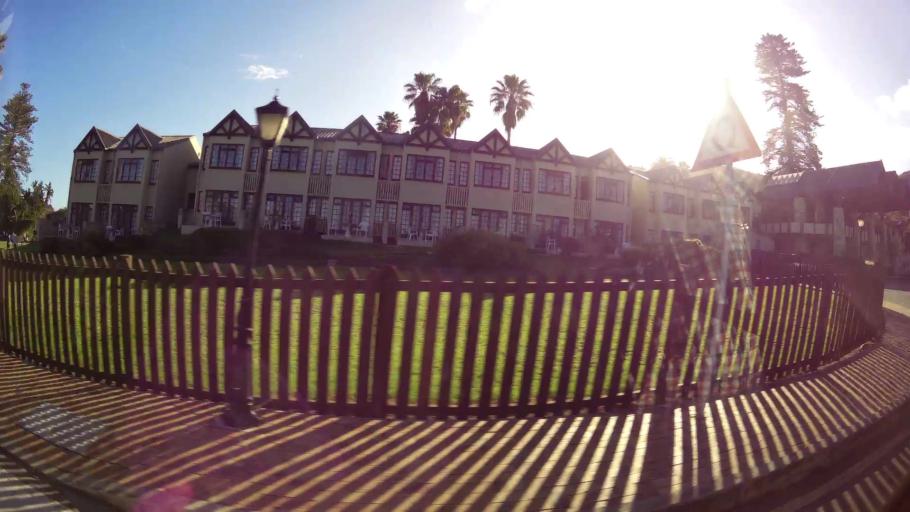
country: ZA
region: Western Cape
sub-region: Eden District Municipality
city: George
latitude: -33.9934
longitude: 22.5774
